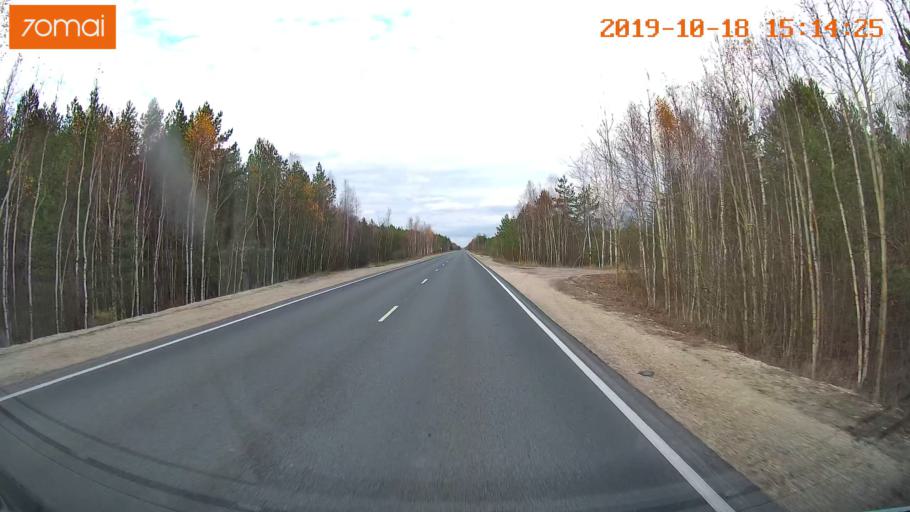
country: RU
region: Vladimir
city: Gus'-Khrustal'nyy
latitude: 55.6024
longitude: 40.7202
